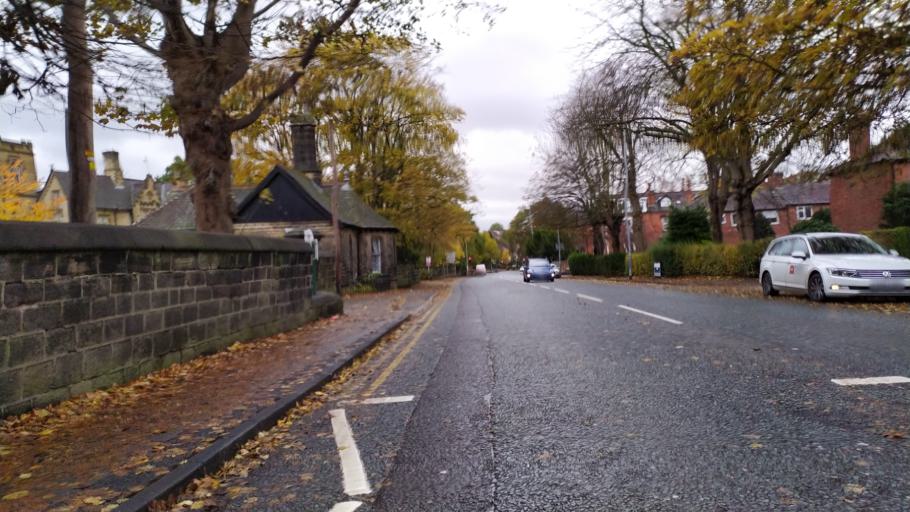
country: GB
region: England
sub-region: City and Borough of Leeds
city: Leeds
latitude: 53.8174
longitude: -1.5871
